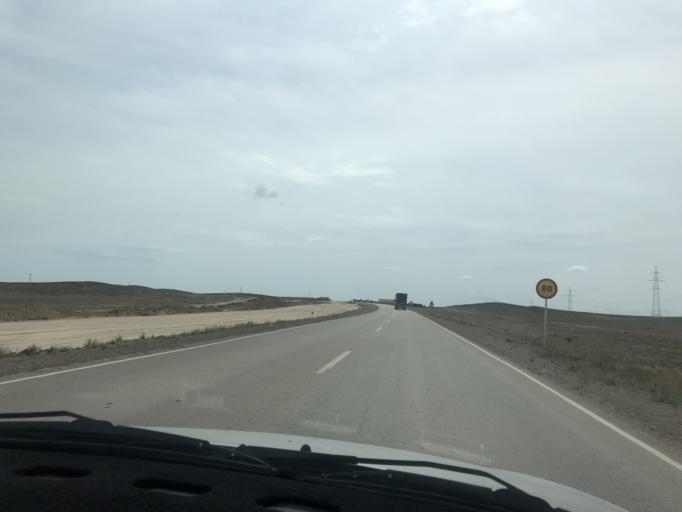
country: KZ
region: Zhambyl
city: Mynaral
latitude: 45.3469
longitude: 73.6927
